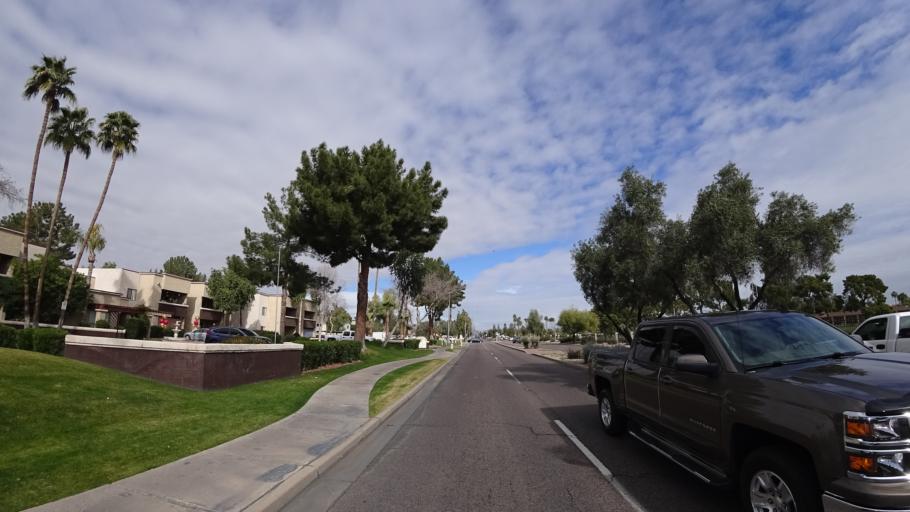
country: US
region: Arizona
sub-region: Maricopa County
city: Peoria
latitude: 33.6220
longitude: -112.1859
